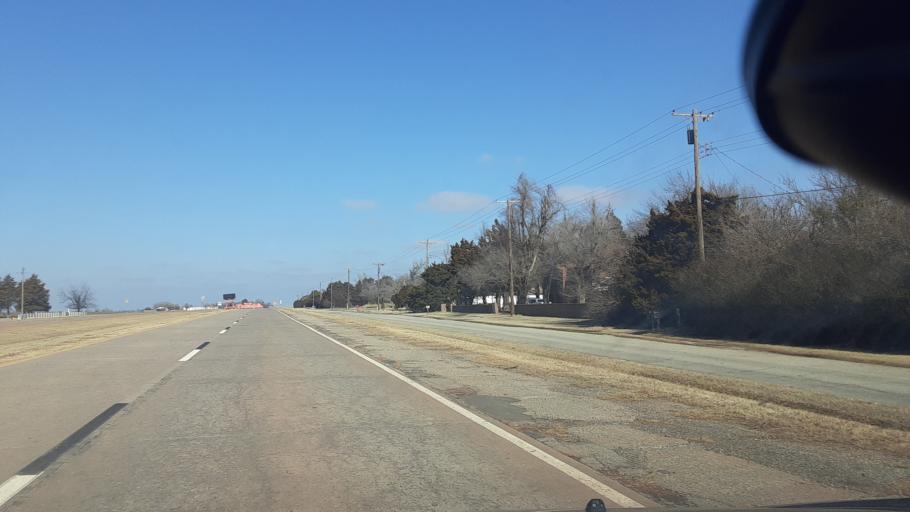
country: US
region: Oklahoma
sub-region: Garfield County
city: Enid
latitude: 36.4543
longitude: -97.8729
